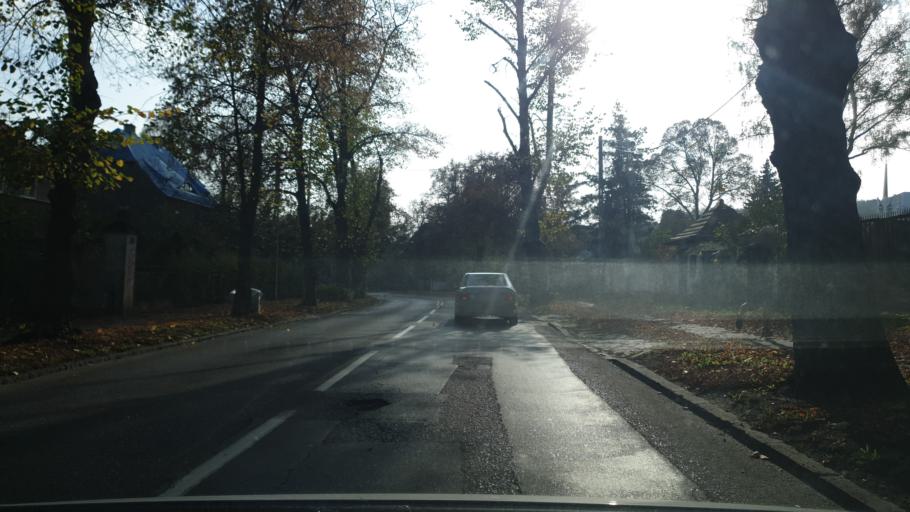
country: PL
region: Pomeranian Voivodeship
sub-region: Sopot
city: Sopot
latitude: 54.3924
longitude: 18.5689
